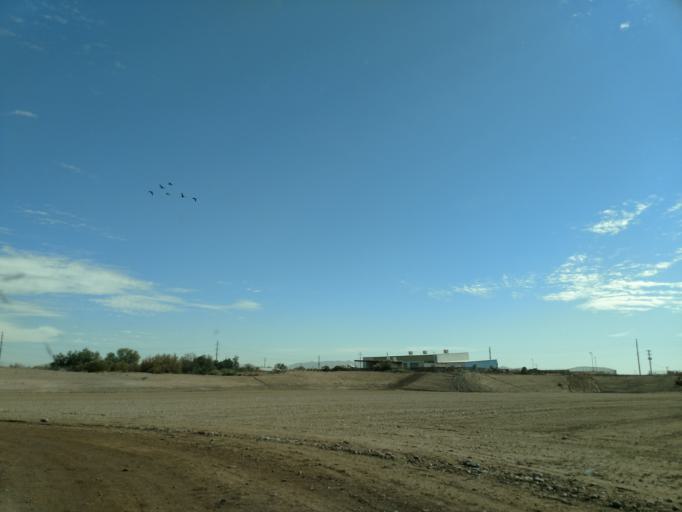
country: US
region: Arizona
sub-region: Maricopa County
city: Laveen
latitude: 33.3945
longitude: -112.1908
